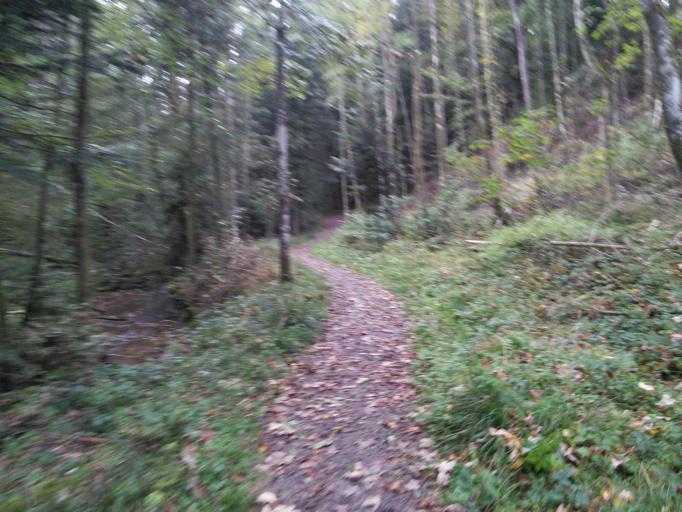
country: DE
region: Baden-Wuerttemberg
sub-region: Regierungsbezirk Stuttgart
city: Welzheim
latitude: 48.8774
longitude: 9.6114
